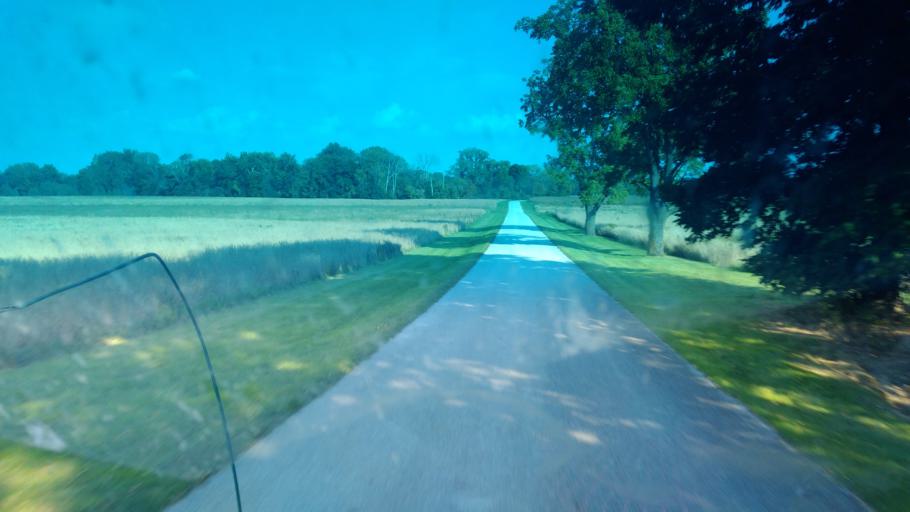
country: US
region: Ohio
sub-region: Wyandot County
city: Upper Sandusky
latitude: 40.9300
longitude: -83.2596
